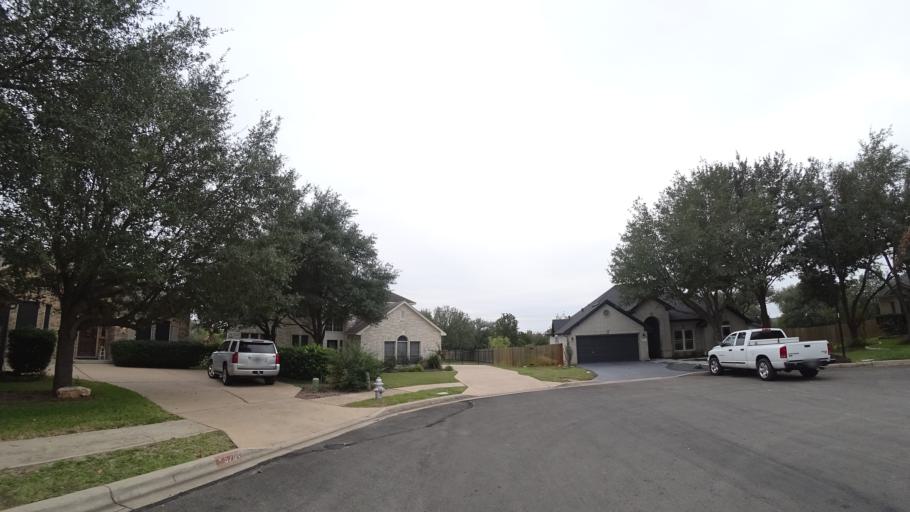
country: US
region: Texas
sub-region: Travis County
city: Shady Hollow
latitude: 30.1827
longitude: -97.8869
